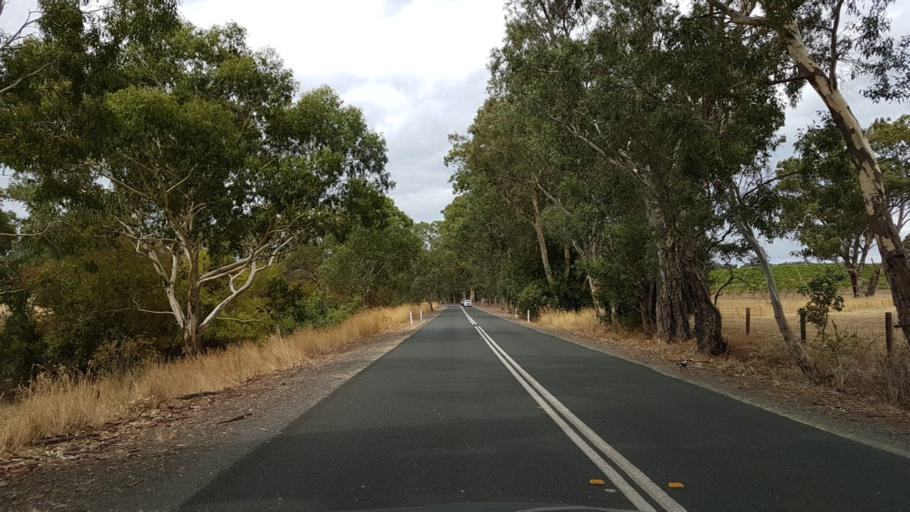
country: AU
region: South Australia
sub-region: Adelaide Hills
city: Gumeracha
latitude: -34.7842
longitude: 138.9099
